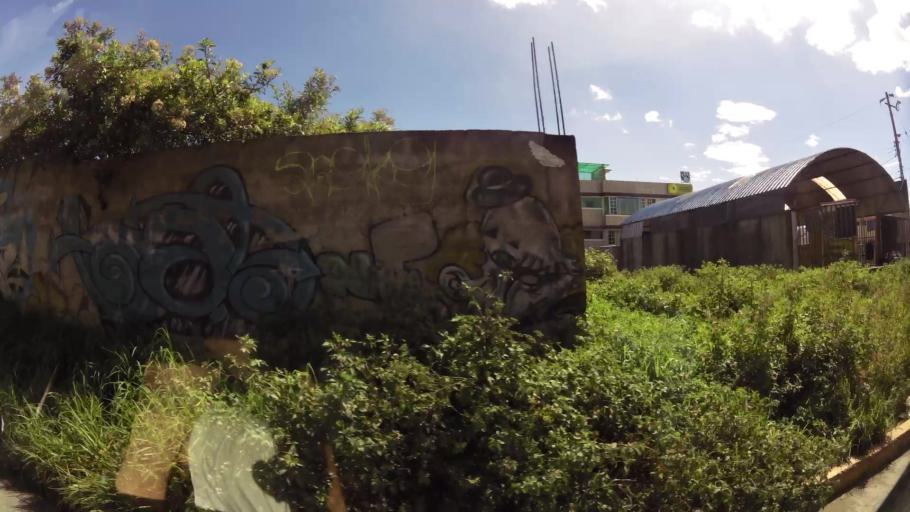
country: EC
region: Pichincha
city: Quito
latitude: -0.3032
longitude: -78.5497
